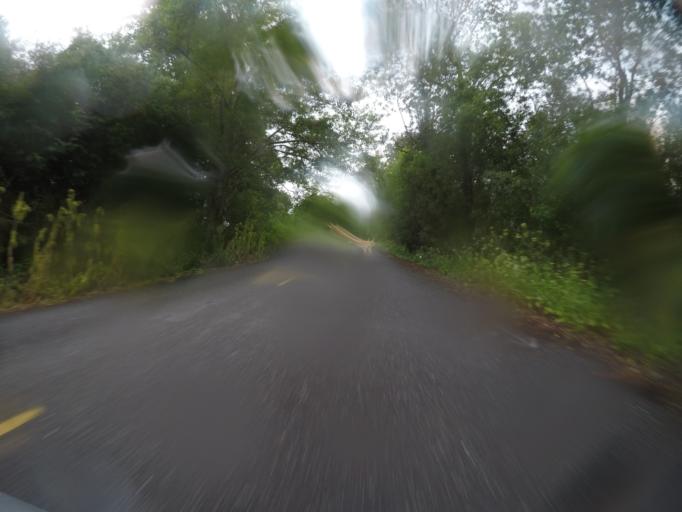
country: US
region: California
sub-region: Humboldt County
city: Westhaven-Moonstone
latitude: 41.3002
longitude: -124.0421
